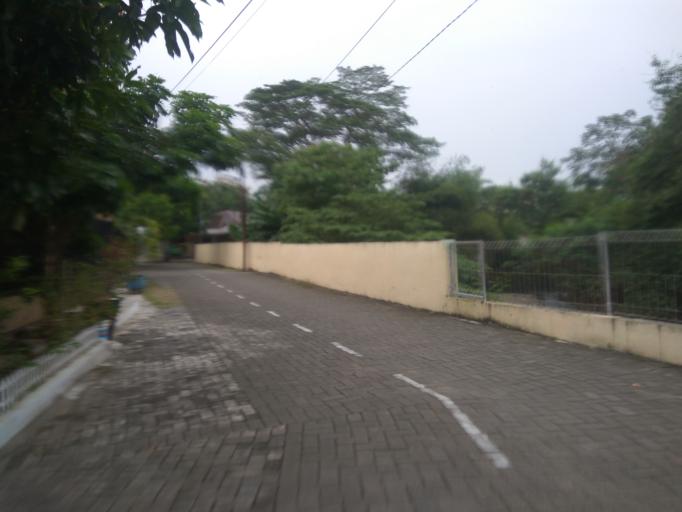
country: ID
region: Central Java
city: Mranggen
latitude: -7.0253
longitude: 110.4650
